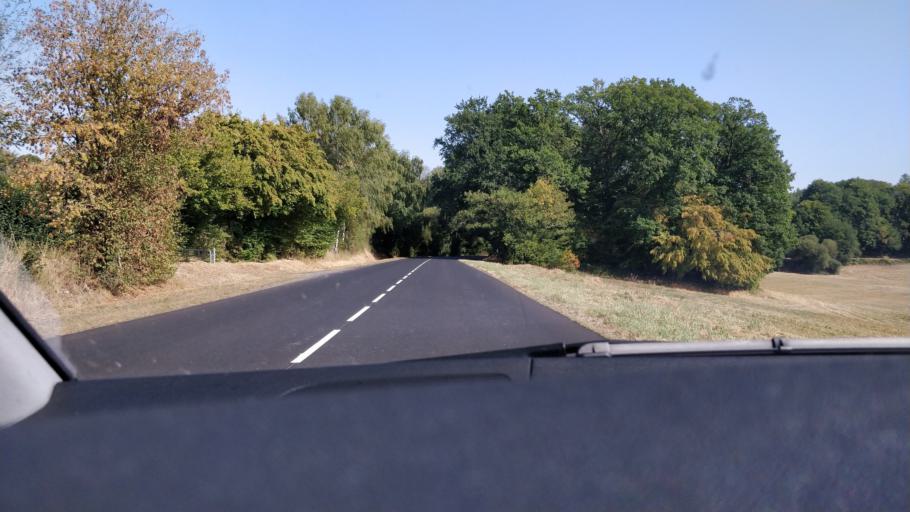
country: FR
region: Limousin
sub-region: Departement de la Correze
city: Uzerche
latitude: 45.4716
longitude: 1.5440
